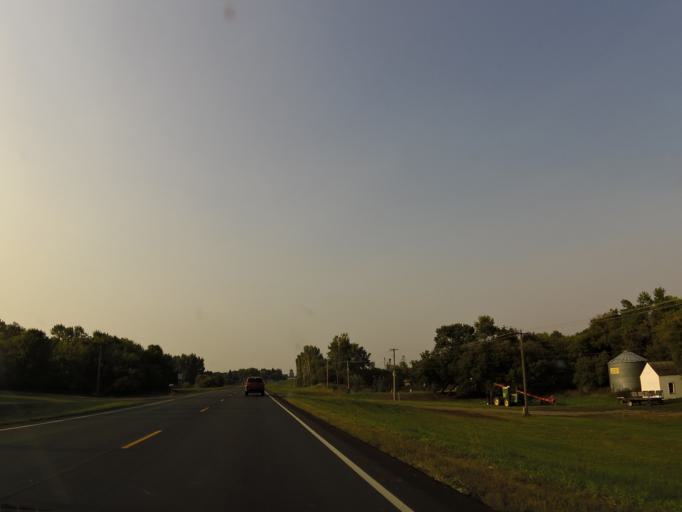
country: US
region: North Dakota
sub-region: Traill County
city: Mayville
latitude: 47.4898
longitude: -97.3230
